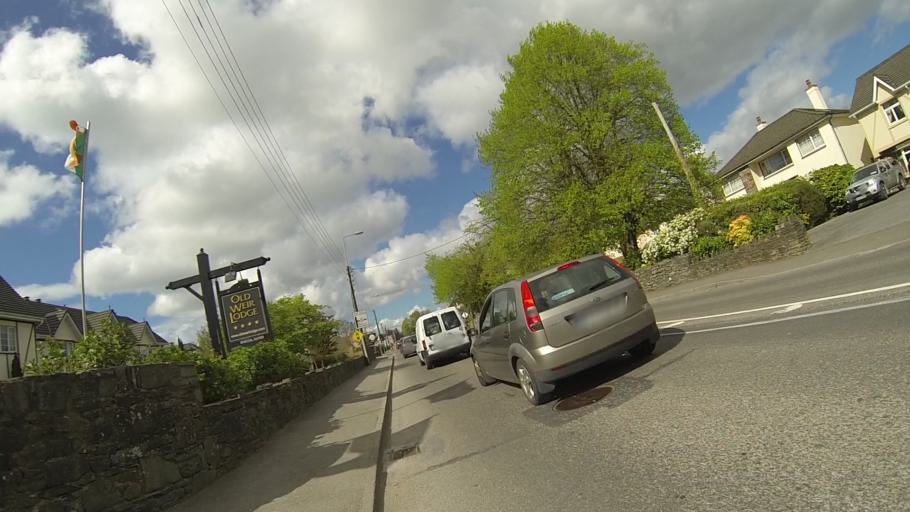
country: IE
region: Munster
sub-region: Ciarrai
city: Cill Airne
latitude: 52.0515
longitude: -9.5068
